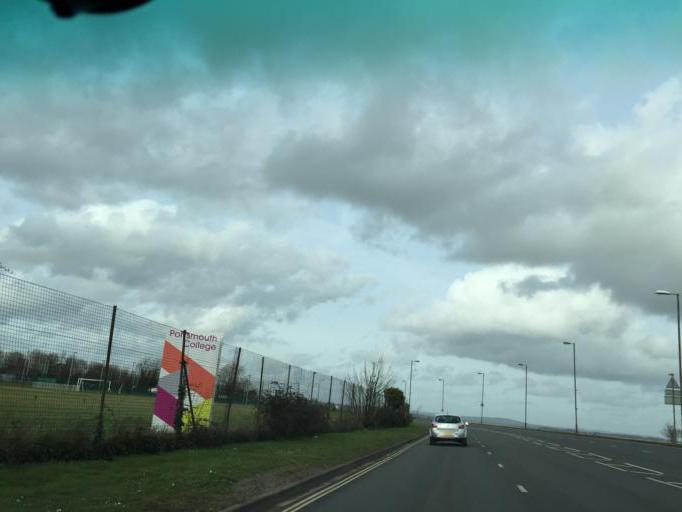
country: GB
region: England
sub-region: Portsmouth
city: Cosham
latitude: 50.8072
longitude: -1.0441
